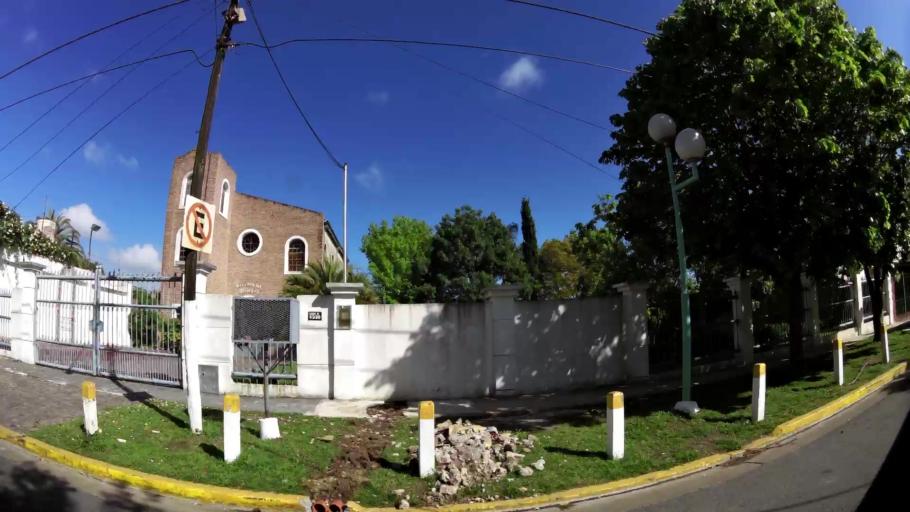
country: AR
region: Buenos Aires
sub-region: Partido de Quilmes
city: Quilmes
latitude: -34.7901
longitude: -58.1504
